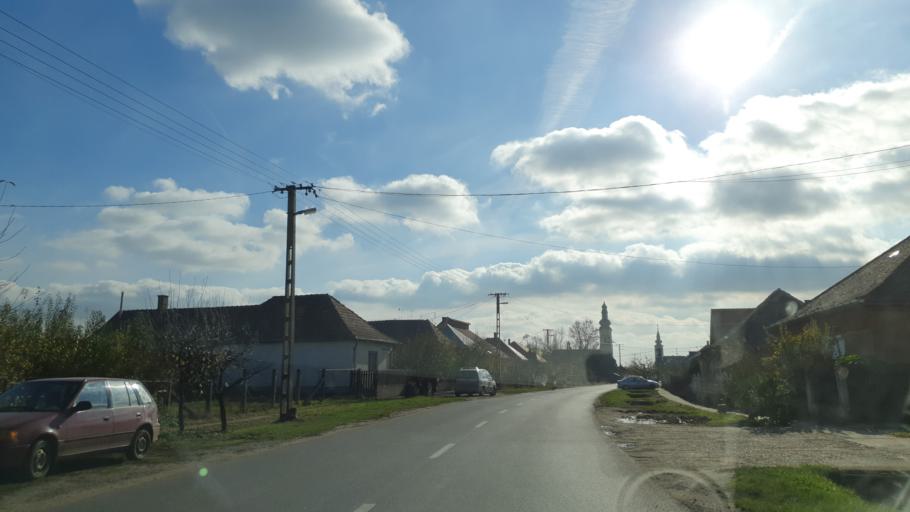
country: HU
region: Szabolcs-Szatmar-Bereg
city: Nyirkarasz
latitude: 48.1058
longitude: 22.0954
